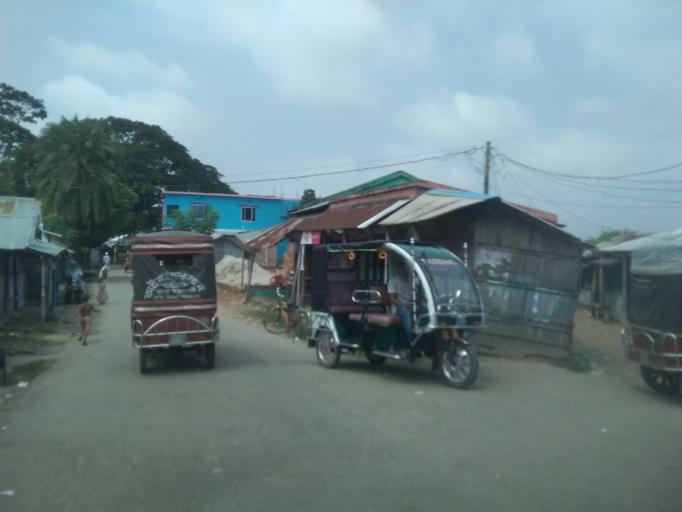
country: BD
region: Khulna
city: Phultala
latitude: 22.6998
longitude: 89.4535
